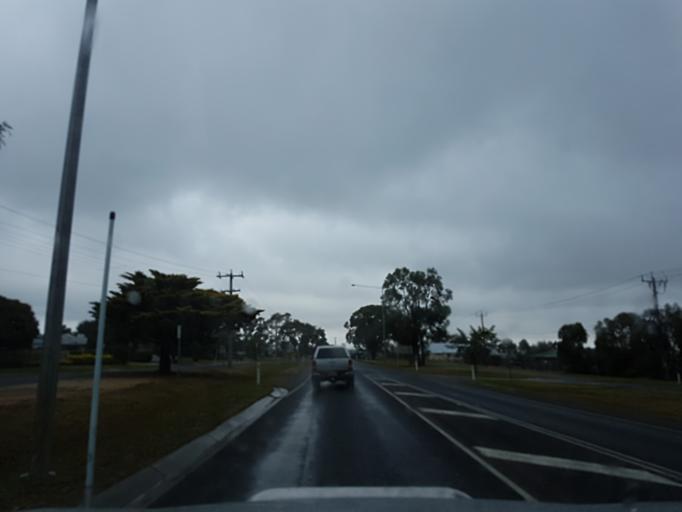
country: AU
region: Victoria
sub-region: East Gippsland
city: Bairnsdale
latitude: -37.8096
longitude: 147.6481
